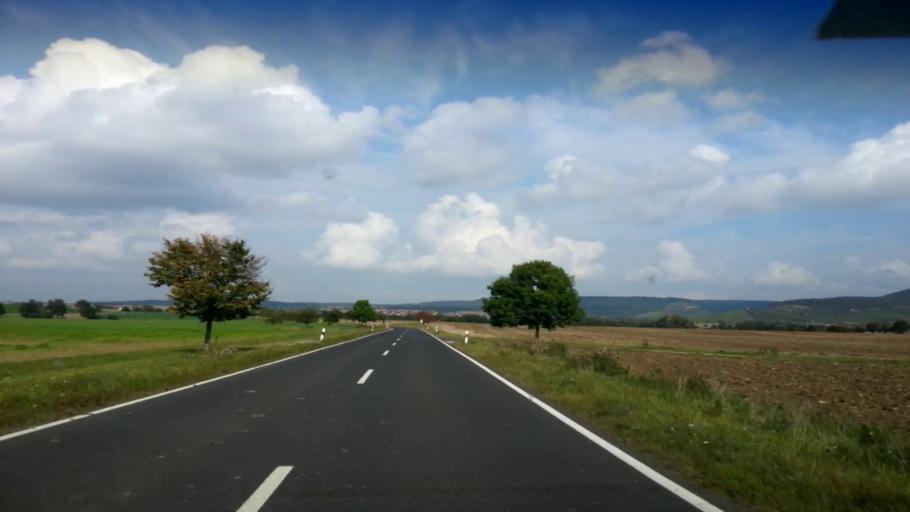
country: DE
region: Bavaria
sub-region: Regierungsbezirk Unterfranken
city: Oberschwarzach
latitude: 49.8437
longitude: 10.4073
